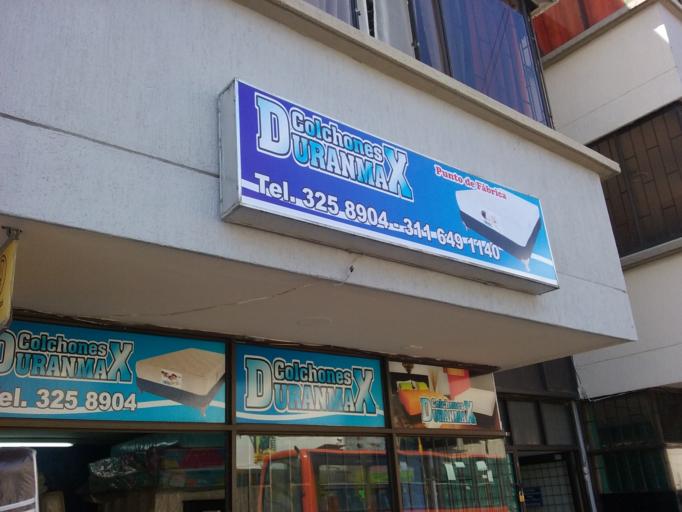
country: CO
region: Risaralda
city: Pereira
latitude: 4.8147
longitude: -75.7001
